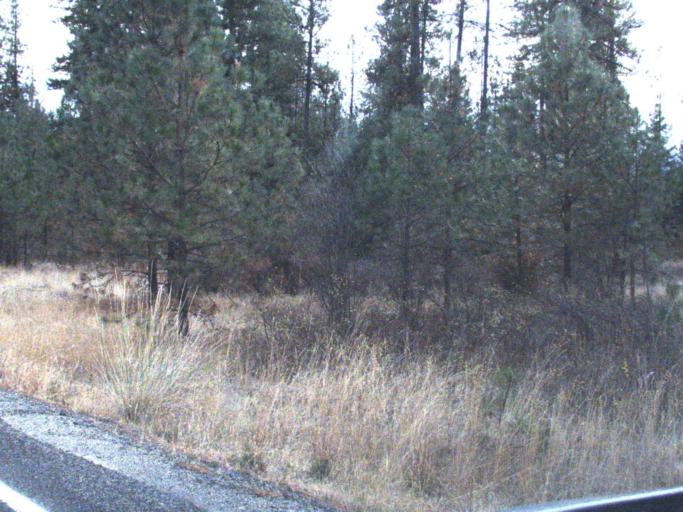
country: US
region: Washington
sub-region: Lincoln County
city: Davenport
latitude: 48.0845
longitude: -118.2027
